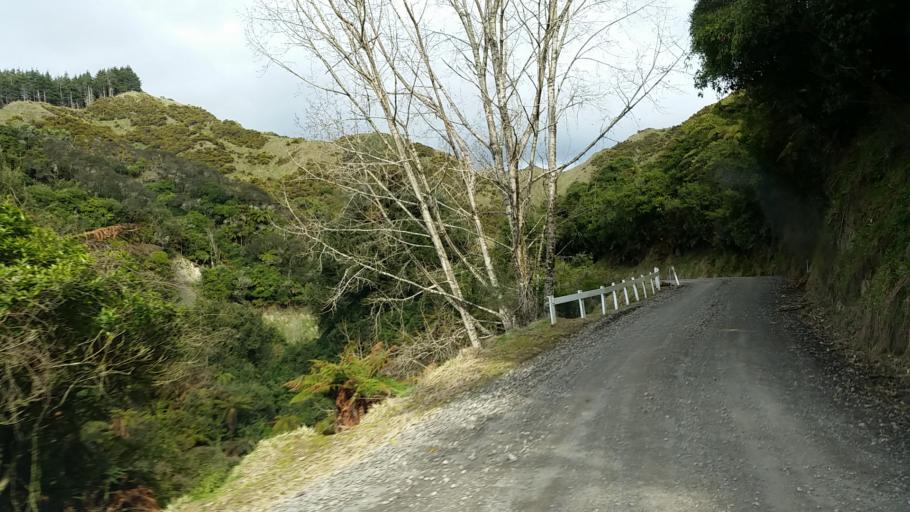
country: NZ
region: Taranaki
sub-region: South Taranaki District
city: Eltham
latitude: -39.1703
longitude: 174.6103
